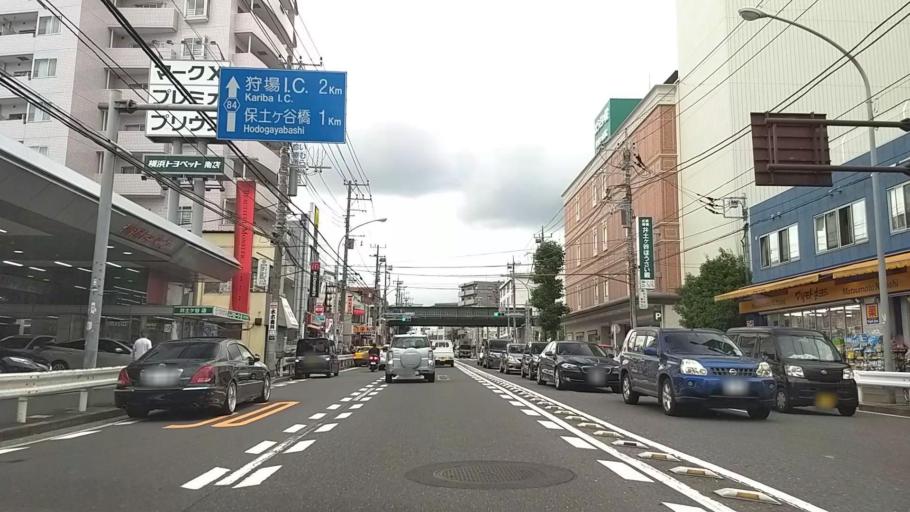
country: JP
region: Kanagawa
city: Yokohama
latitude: 35.4333
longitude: 139.6019
